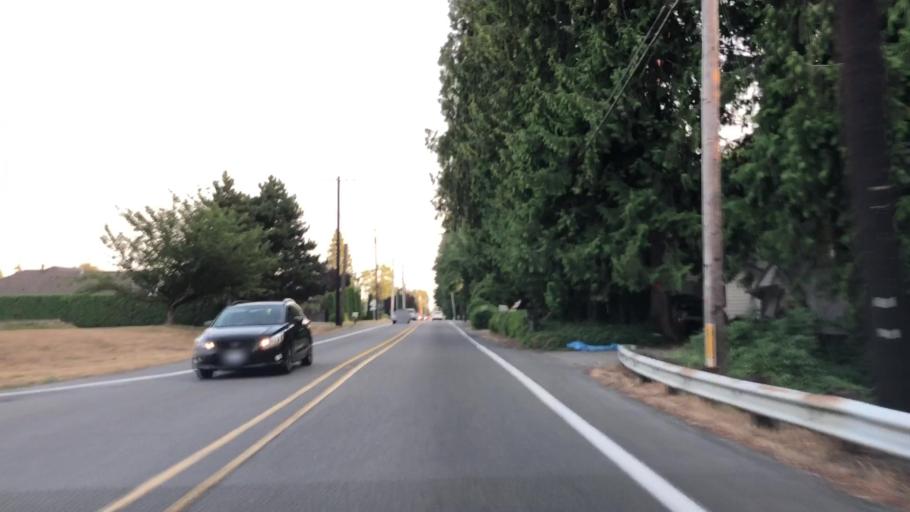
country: US
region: Washington
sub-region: Snohomish County
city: Marysville
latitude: 48.0997
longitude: -122.1623
